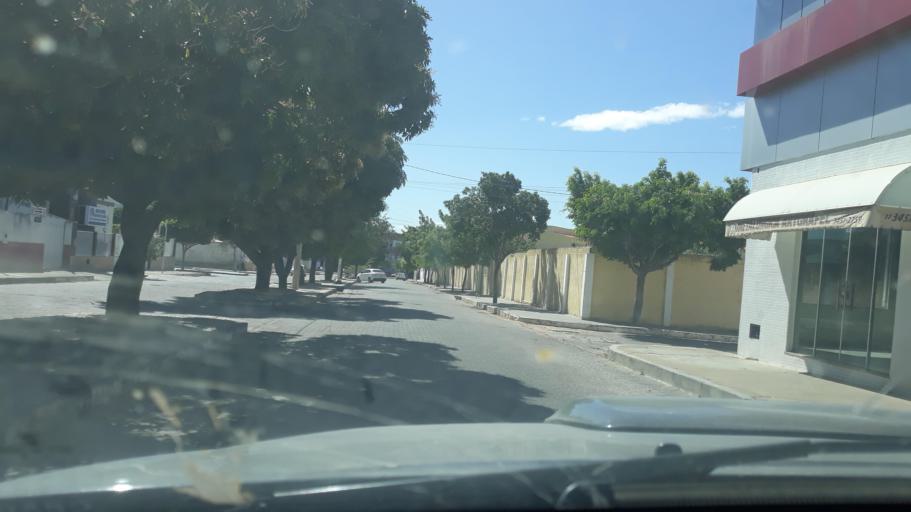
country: BR
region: Bahia
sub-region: Guanambi
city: Guanambi
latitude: -14.2186
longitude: -42.7840
